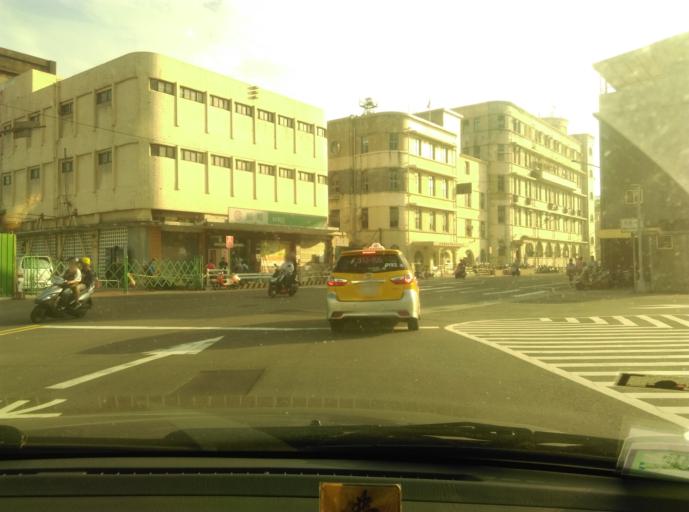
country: TW
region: Taiwan
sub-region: Keelung
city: Keelung
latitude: 25.1342
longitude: 121.7407
